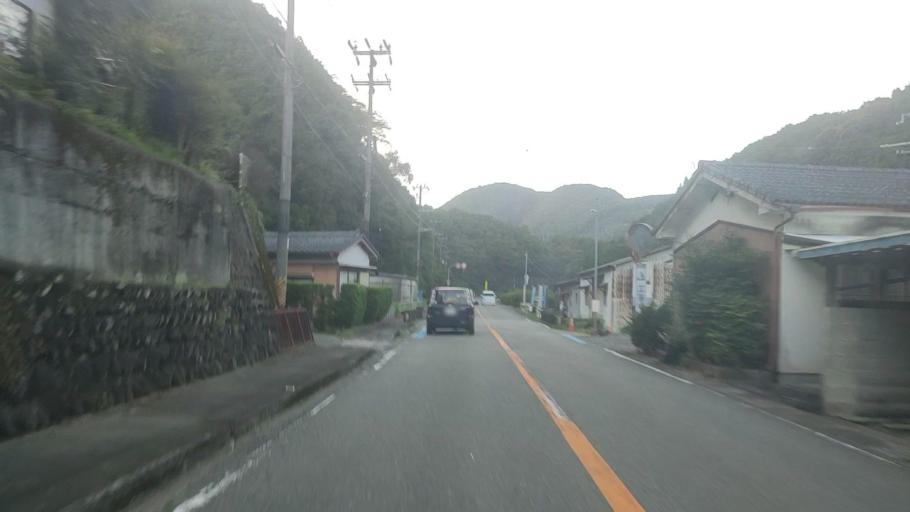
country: JP
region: Wakayama
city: Tanabe
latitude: 33.7957
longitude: 135.5189
